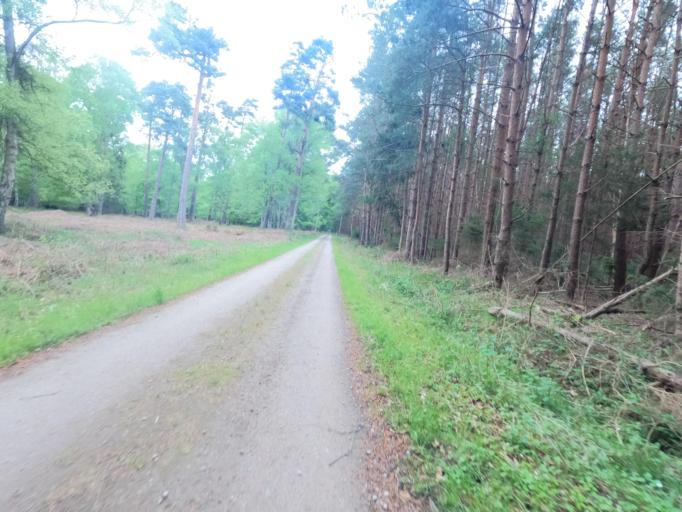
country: DE
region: Mecklenburg-Vorpommern
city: Born
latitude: 54.4107
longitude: 12.4953
